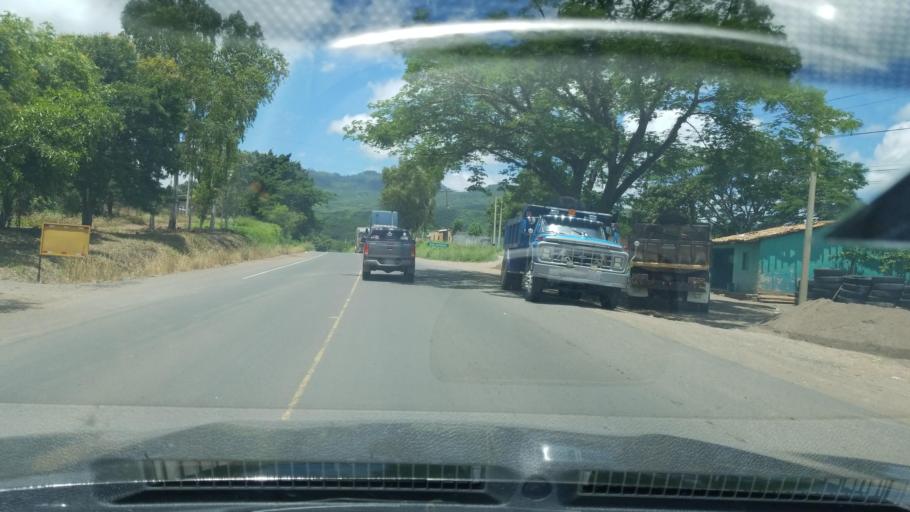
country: HN
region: Francisco Morazan
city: Cofradia
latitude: 14.2609
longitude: -87.2452
